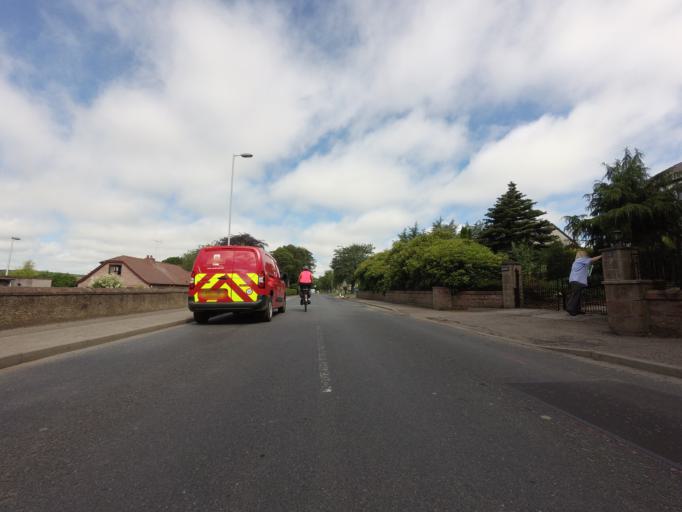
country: GB
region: Scotland
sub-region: Aberdeenshire
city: Turriff
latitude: 57.5401
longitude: -2.4707
